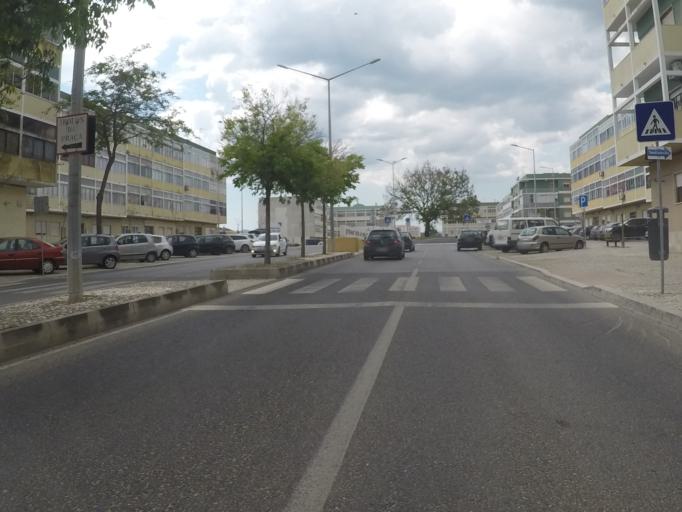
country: PT
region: Setubal
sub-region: Setubal
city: Setubal
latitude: 38.5254
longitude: -8.8738
